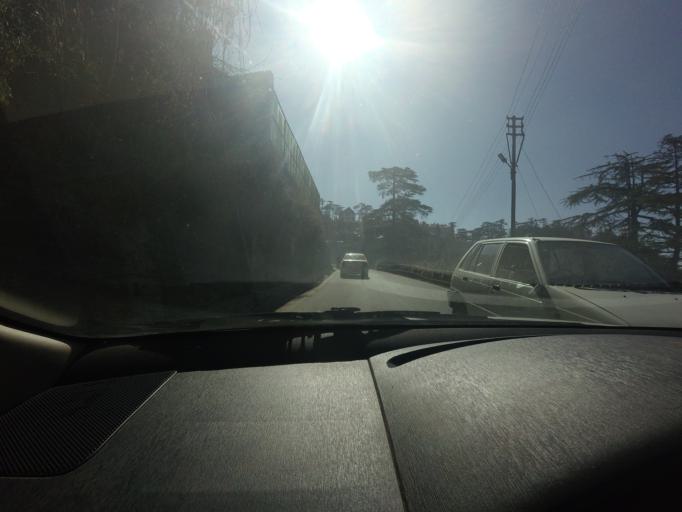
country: IN
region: Himachal Pradesh
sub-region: Shimla
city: Shimla
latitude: 31.1077
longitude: 77.1654
